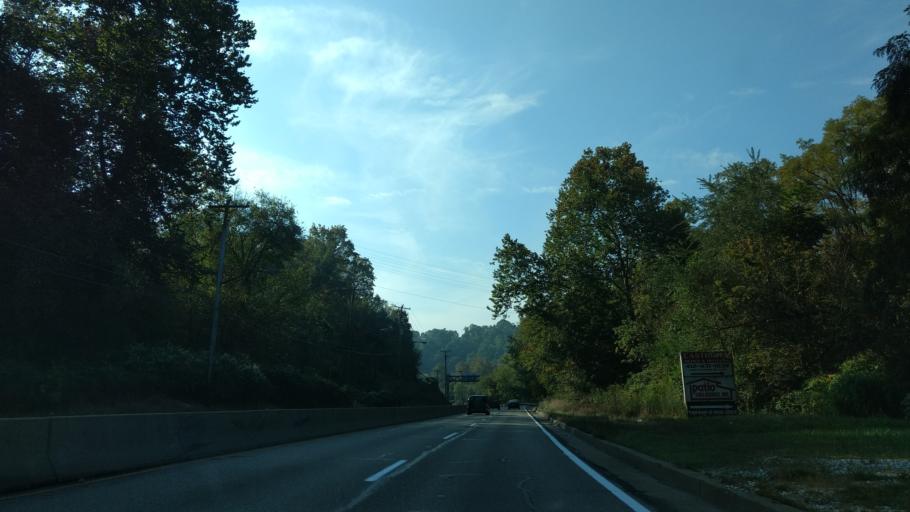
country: US
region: Pennsylvania
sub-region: Allegheny County
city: Pittsburgh
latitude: 40.4204
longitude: -80.0153
